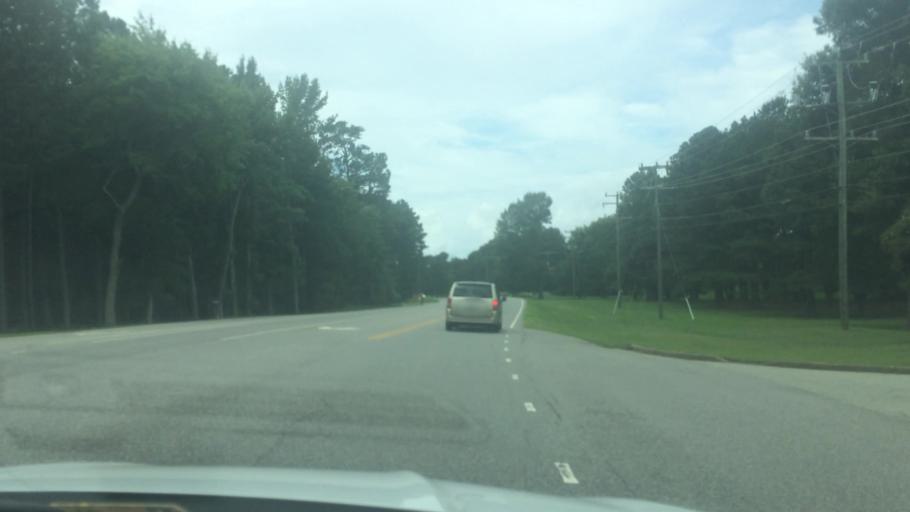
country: US
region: Virginia
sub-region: James City County
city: Williamsburg
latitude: 37.2646
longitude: -76.7606
